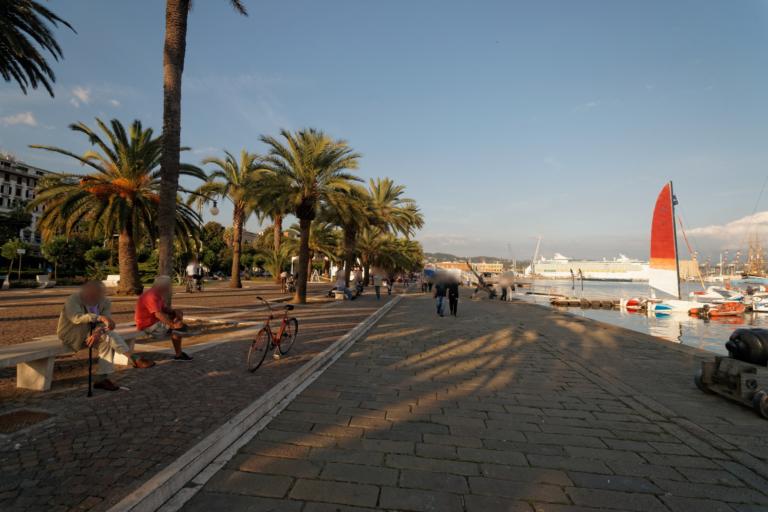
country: IT
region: Liguria
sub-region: Provincia di La Spezia
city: La Spezia
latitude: 44.1038
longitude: 9.8264
